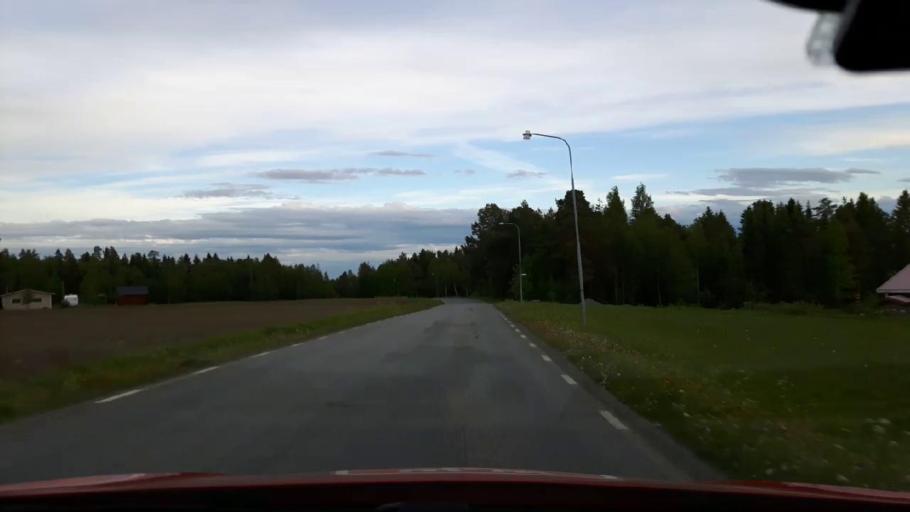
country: SE
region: Jaemtland
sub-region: Bergs Kommun
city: Hoverberg
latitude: 63.0274
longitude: 14.4748
